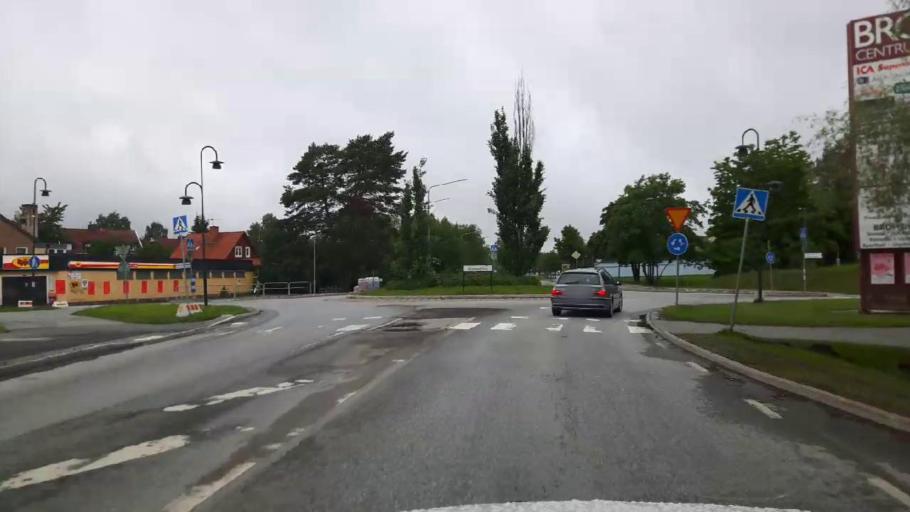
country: SE
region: Stockholm
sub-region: Upplands-Bro Kommun
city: Bro
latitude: 59.5147
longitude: 17.6411
